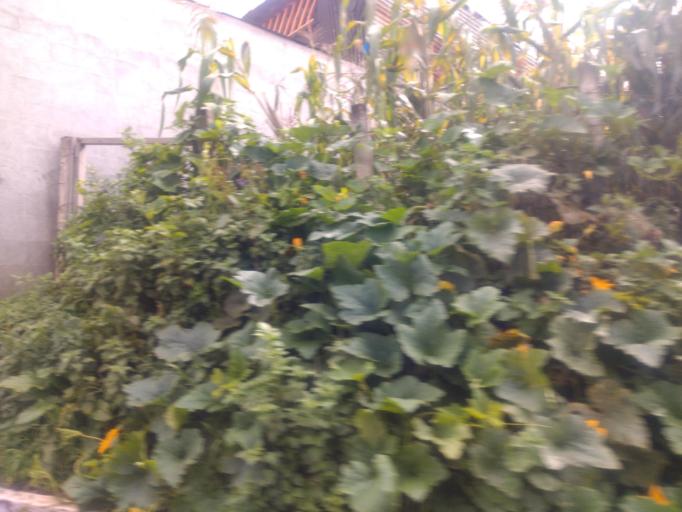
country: GT
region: Quetzaltenango
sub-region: Municipio de La Esperanza
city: La Esperanza
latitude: 14.8693
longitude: -91.5596
